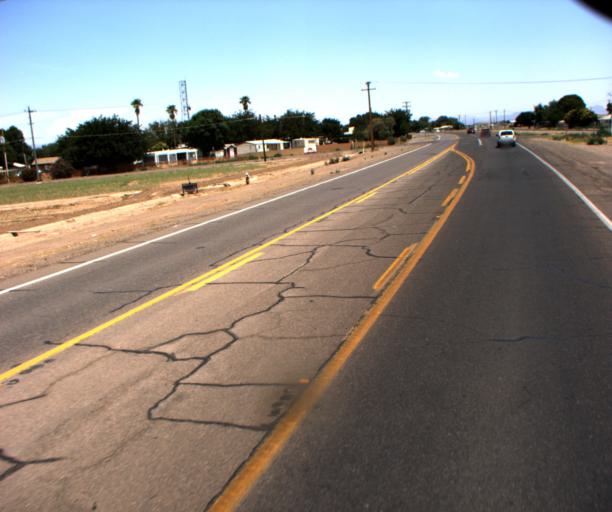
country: US
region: Arizona
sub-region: Graham County
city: Safford
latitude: 32.8185
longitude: -109.6831
